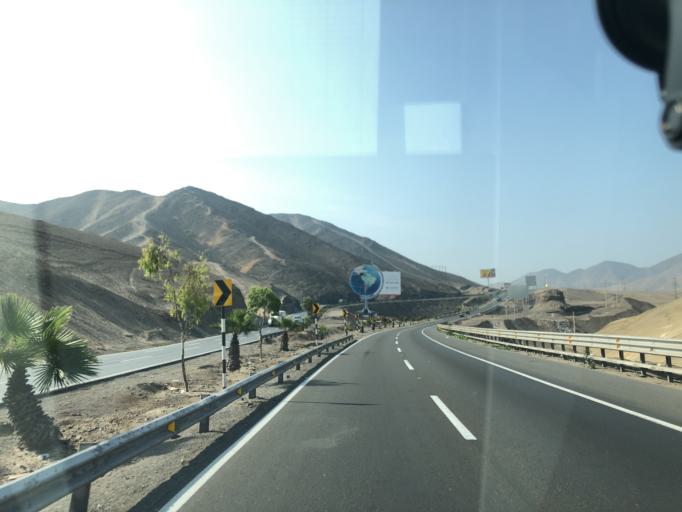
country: PE
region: Lima
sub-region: Lima
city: San Bartolo
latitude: -12.4284
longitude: -76.7535
